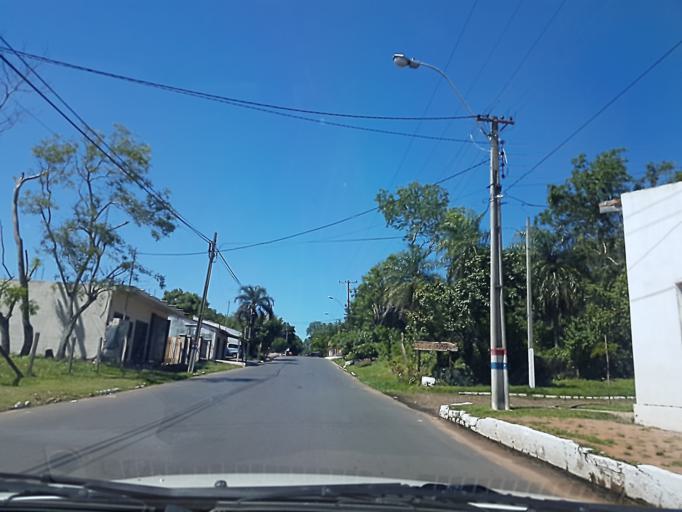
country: PY
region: Cordillera
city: Atyra
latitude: -25.2812
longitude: -57.1751
